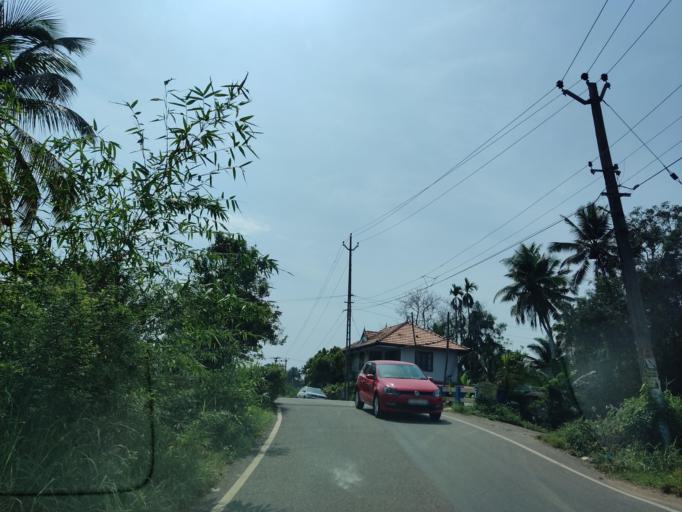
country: IN
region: Kerala
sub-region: Pattanamtitta
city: Tiruvalla
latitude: 9.3390
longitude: 76.4683
